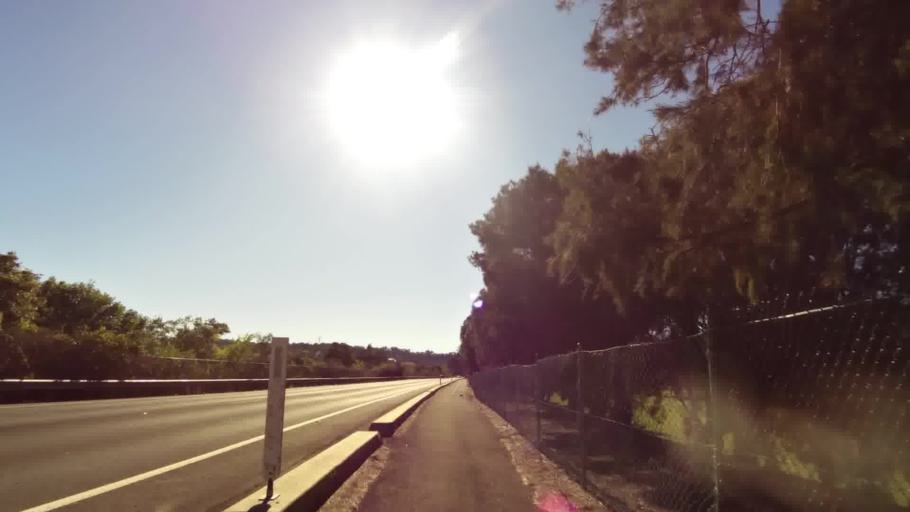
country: AU
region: New South Wales
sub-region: Wollongong
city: Koonawarra
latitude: -34.4786
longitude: 150.8064
